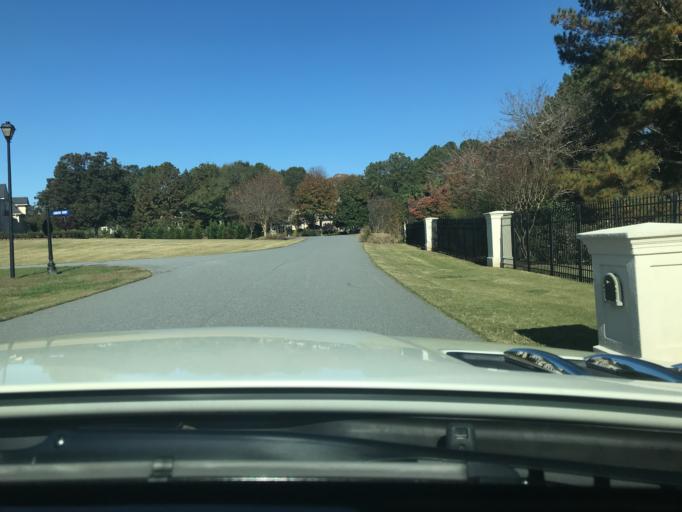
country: US
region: Georgia
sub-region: Gwinnett County
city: Duluth
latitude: 34.0372
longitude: -84.1549
